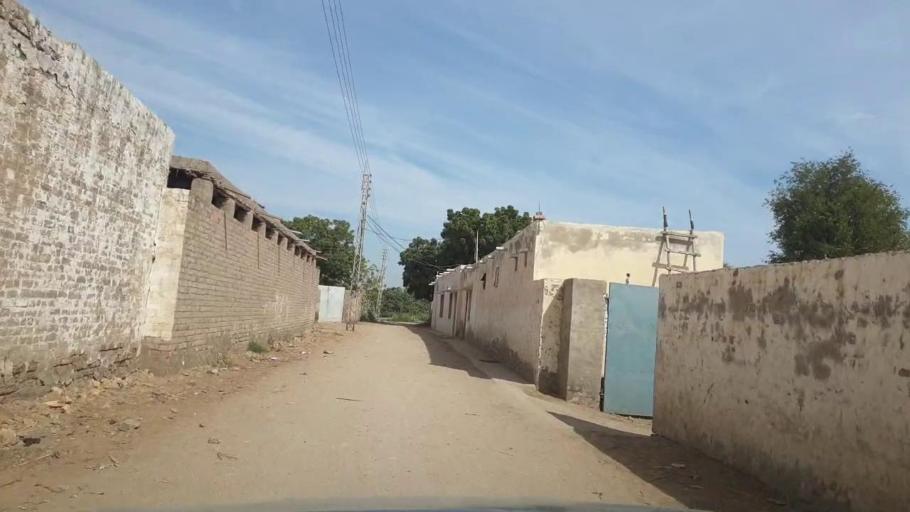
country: PK
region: Sindh
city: Kunri
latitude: 25.1591
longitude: 69.5911
